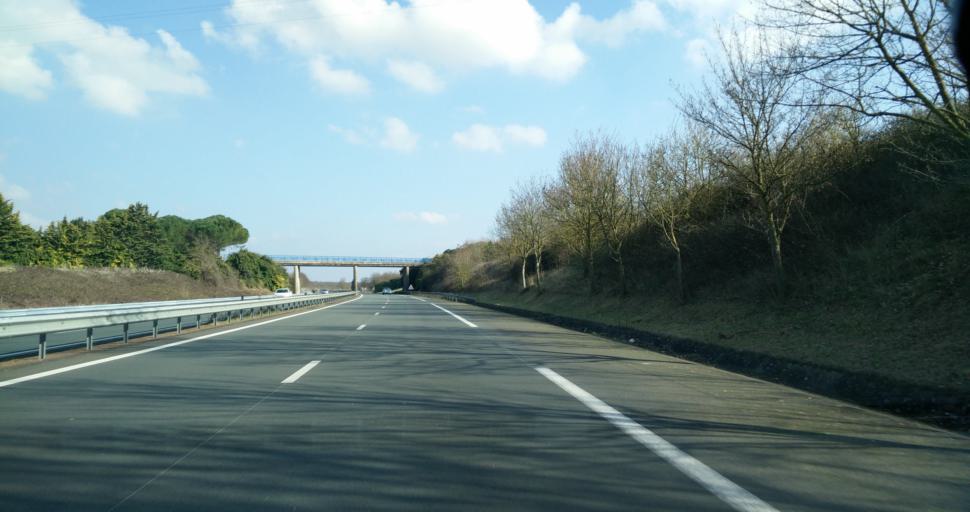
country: FR
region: Poitou-Charentes
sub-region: Departement de la Charente-Maritime
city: Courcon
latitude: 46.2236
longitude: -0.8508
